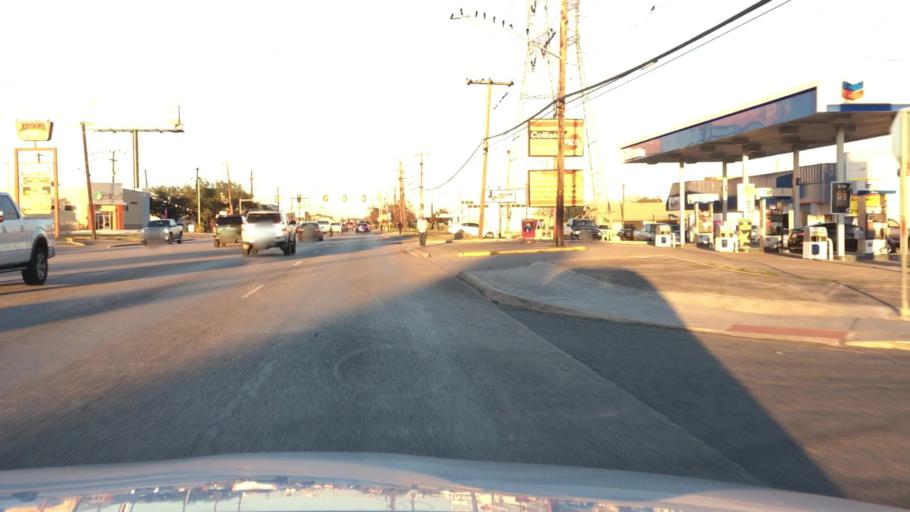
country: US
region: Texas
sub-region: Bexar County
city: Windcrest
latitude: 29.5622
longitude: -98.3924
